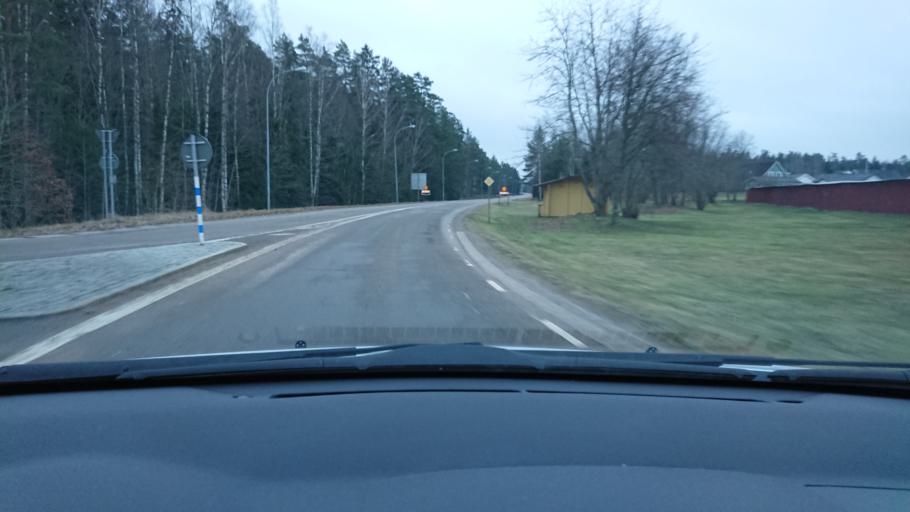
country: SE
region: Kronoberg
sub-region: Vaxjo Kommun
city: Braas
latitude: 57.0596
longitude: 15.0583
